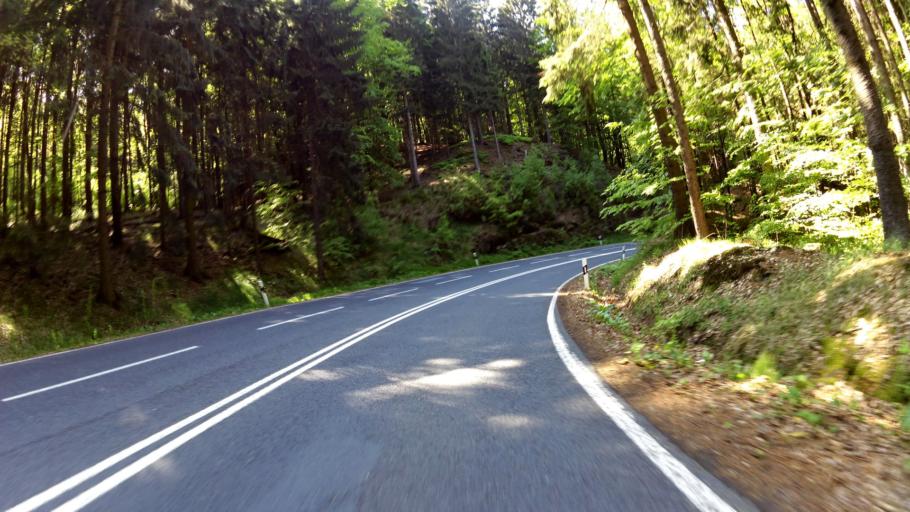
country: DE
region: Saxony
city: Hohnstein
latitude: 50.9819
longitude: 14.0977
